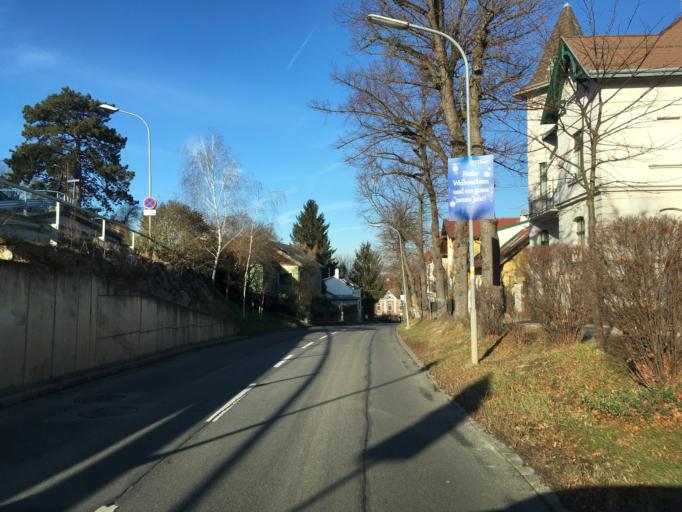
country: AT
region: Lower Austria
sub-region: Politischer Bezirk Korneuburg
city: Korneuburg
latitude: 48.3332
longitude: 16.2991
